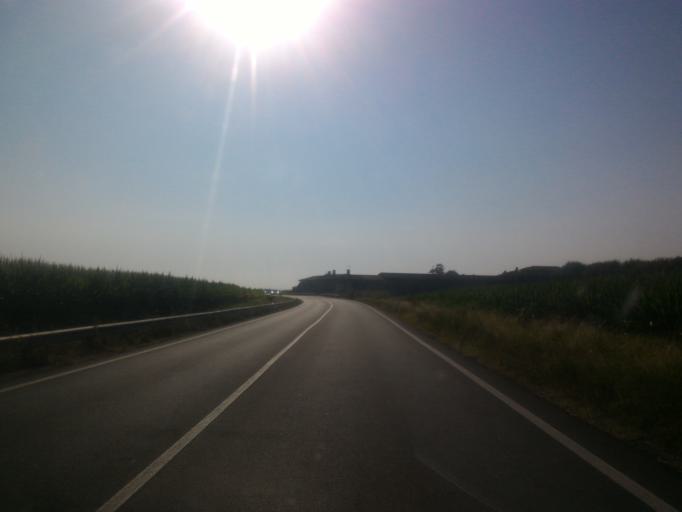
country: IT
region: Piedmont
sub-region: Provincia di Torino
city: Riva
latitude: 44.8784
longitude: 7.3702
